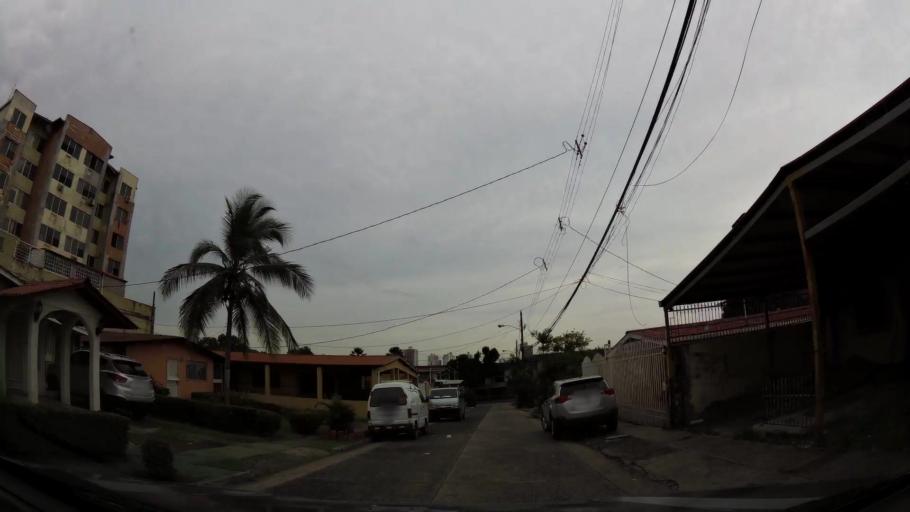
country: PA
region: Panama
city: Panama
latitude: 9.0220
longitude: -79.5268
